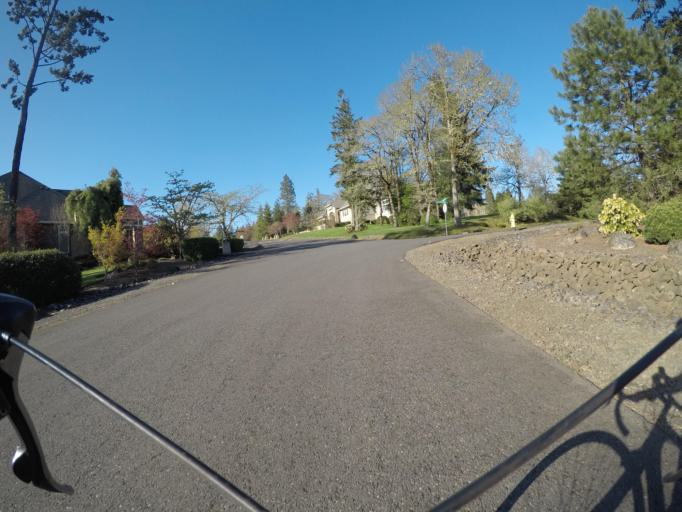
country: US
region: Oregon
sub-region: Washington County
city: Aloha
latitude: 45.4500
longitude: -122.8804
